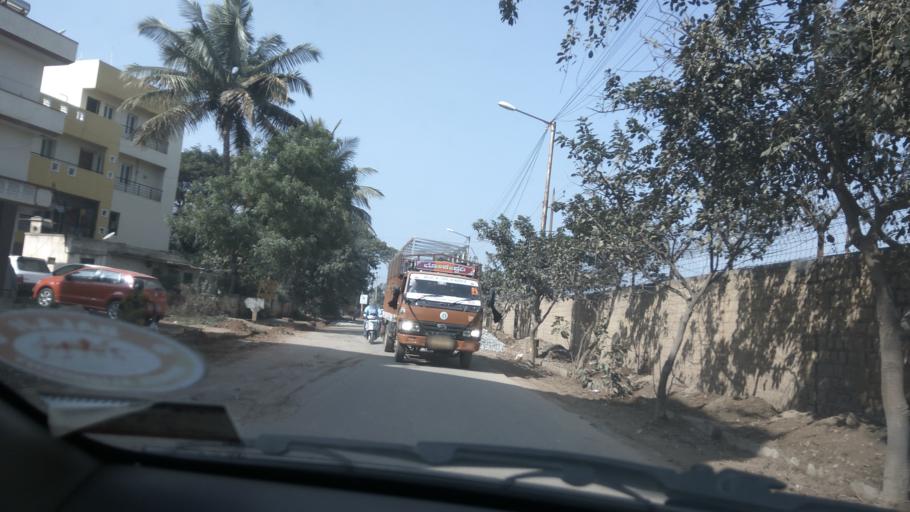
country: IN
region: Karnataka
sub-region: Bangalore Urban
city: Bangalore
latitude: 12.9486
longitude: 77.6818
